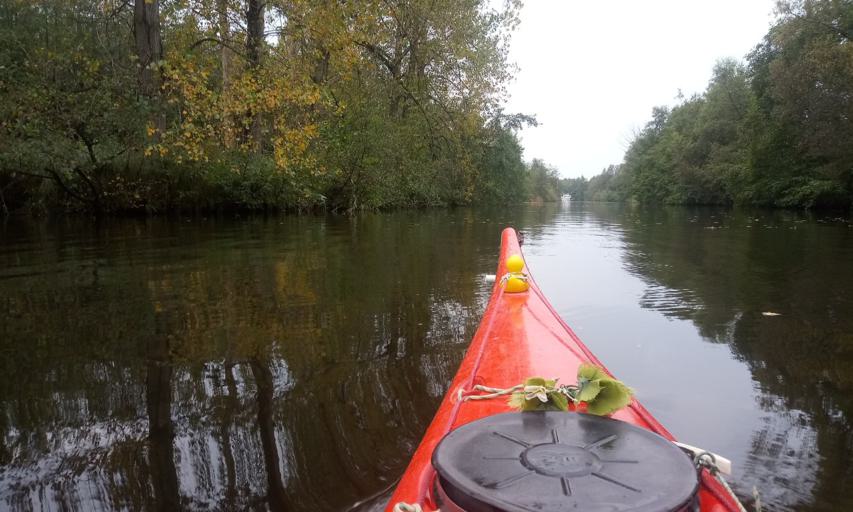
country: NL
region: North Holland
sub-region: Gemeente Wijdemeren
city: Oud-Loosdrecht
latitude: 52.2007
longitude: 5.1049
